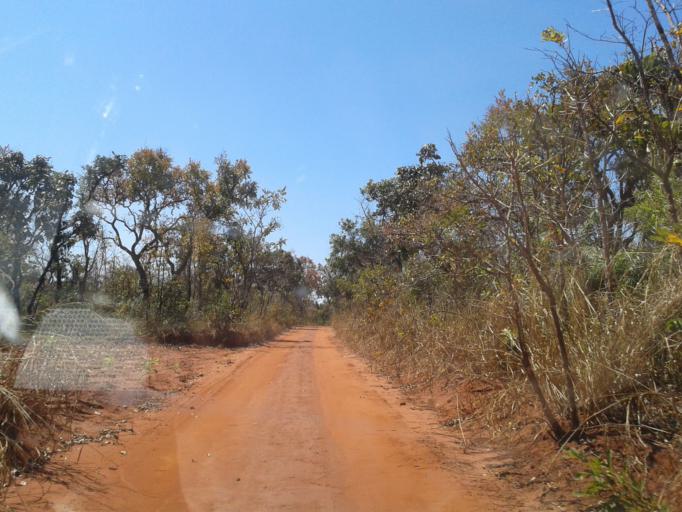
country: BR
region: Minas Gerais
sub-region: Monte Alegre De Minas
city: Monte Alegre de Minas
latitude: -18.8278
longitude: -49.1081
